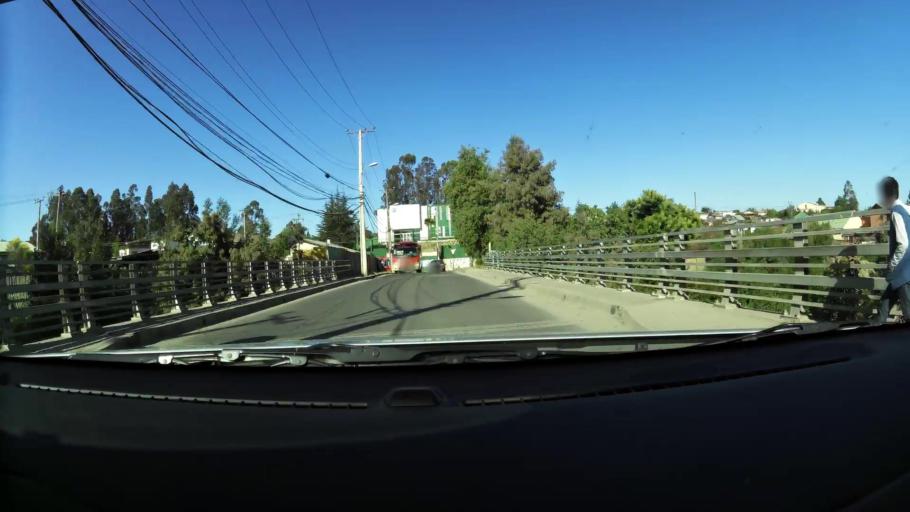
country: CL
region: Valparaiso
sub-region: Provincia de Valparaiso
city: Valparaiso
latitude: -33.1150
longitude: -71.5773
